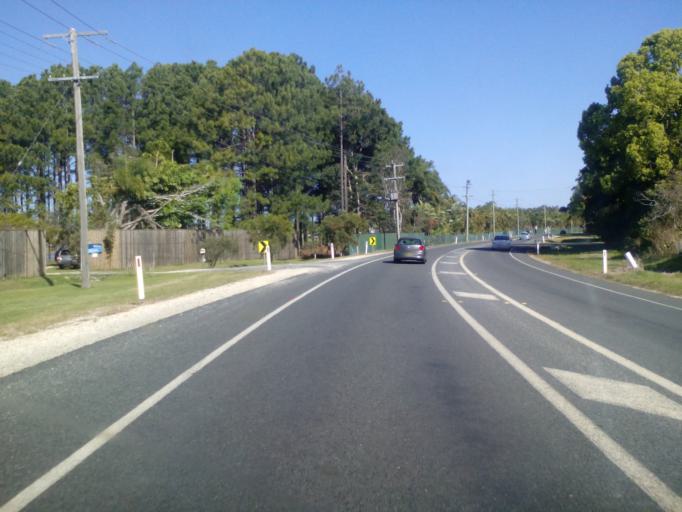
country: AU
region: New South Wales
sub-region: Tweed
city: Kingscliff
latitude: -28.2527
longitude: 153.5591
